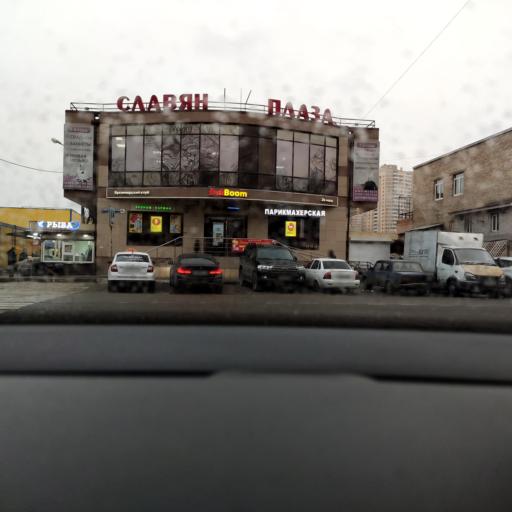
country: RU
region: Moskovskaya
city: Reutov
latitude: 55.7544
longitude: 37.8621
